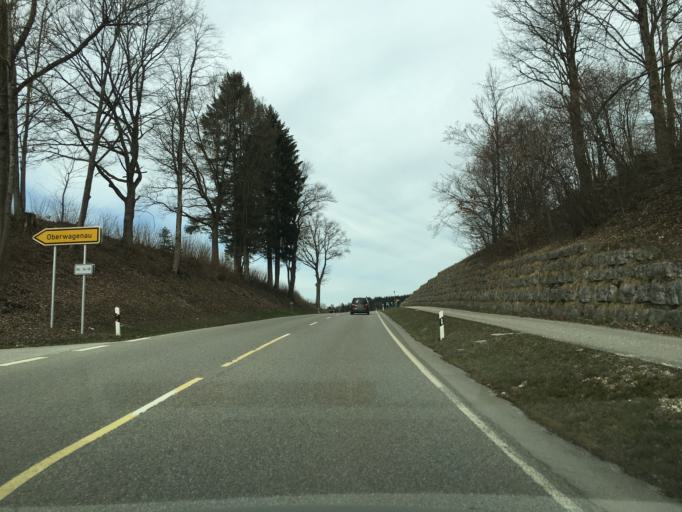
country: DE
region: Bavaria
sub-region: Upper Bavaria
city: Inzell
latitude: 47.7882
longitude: 12.7276
